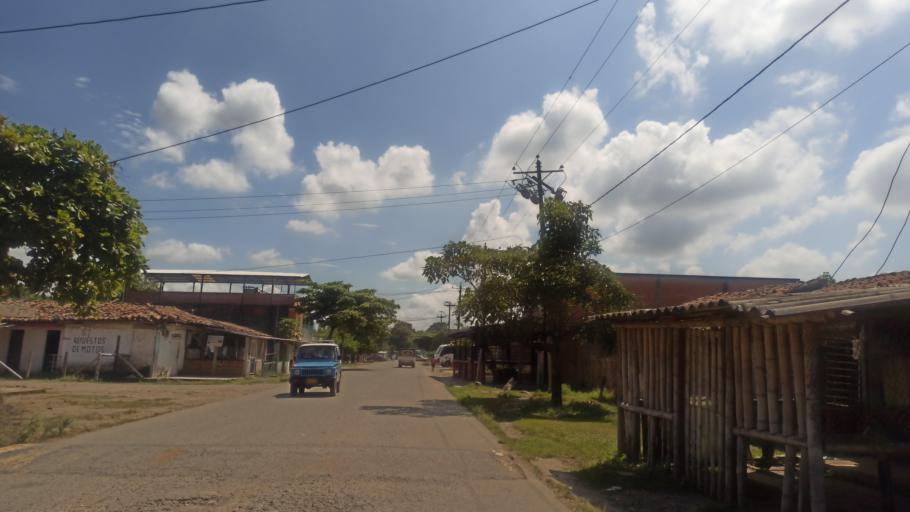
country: CO
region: Valle del Cauca
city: Jamundi
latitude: 3.1336
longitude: -76.5447
